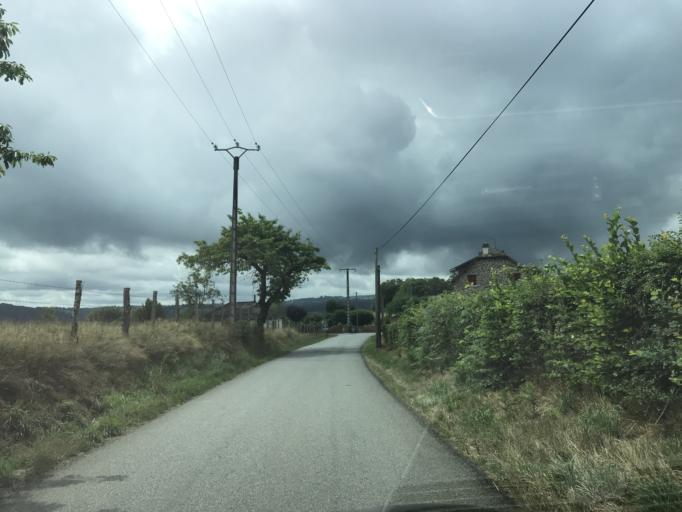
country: FR
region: Auvergne
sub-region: Departement du Cantal
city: Pleaux
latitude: 45.2413
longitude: 2.1950
